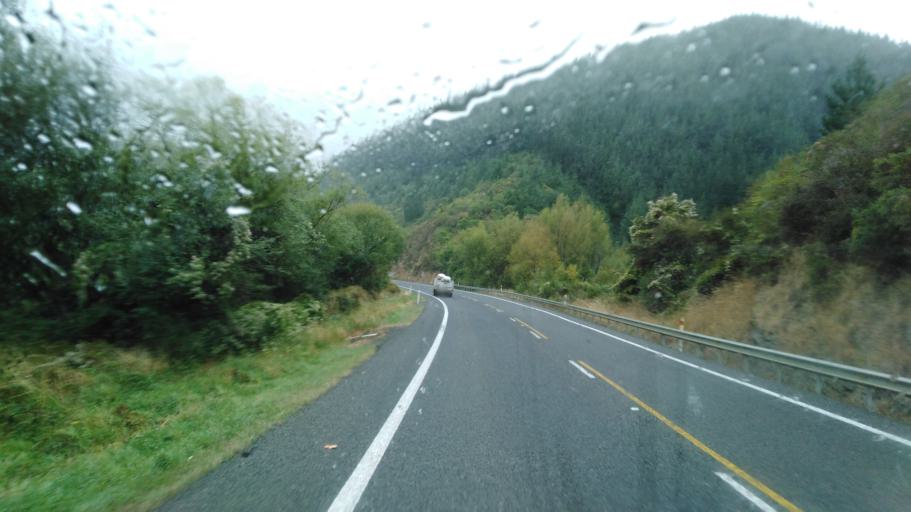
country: NZ
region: Marlborough
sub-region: Marlborough District
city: Picton
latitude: -41.3871
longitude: 173.9520
